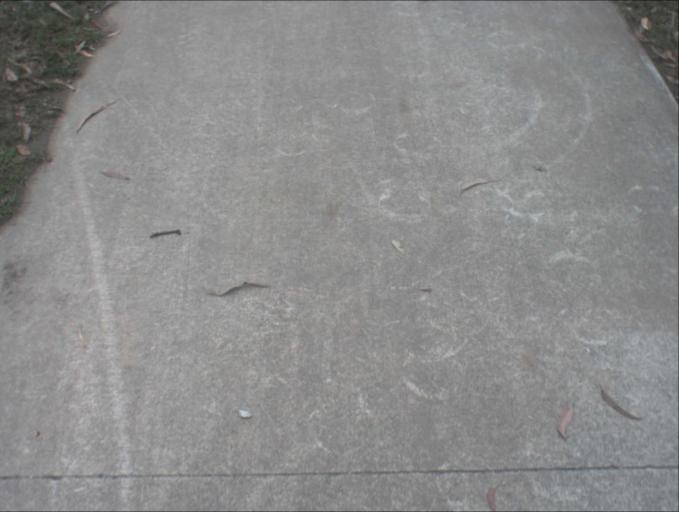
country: AU
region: Queensland
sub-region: Logan
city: Logan Reserve
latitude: -27.6984
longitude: 153.0769
